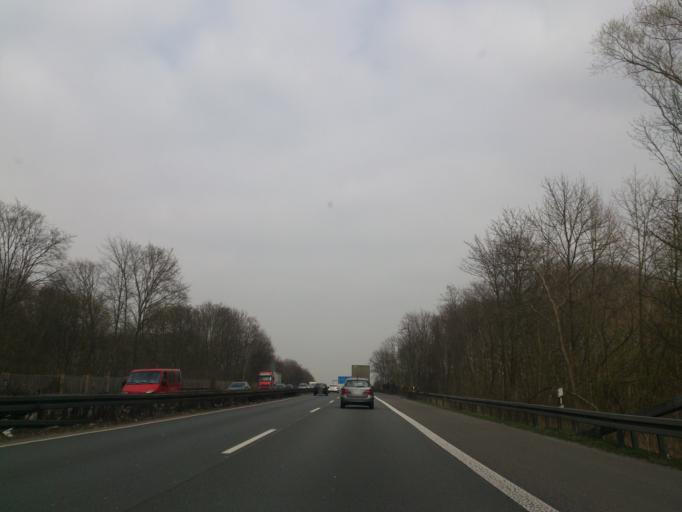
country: DE
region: North Rhine-Westphalia
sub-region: Regierungsbezirk Dusseldorf
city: Monchengladbach
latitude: 51.2355
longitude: 6.4595
